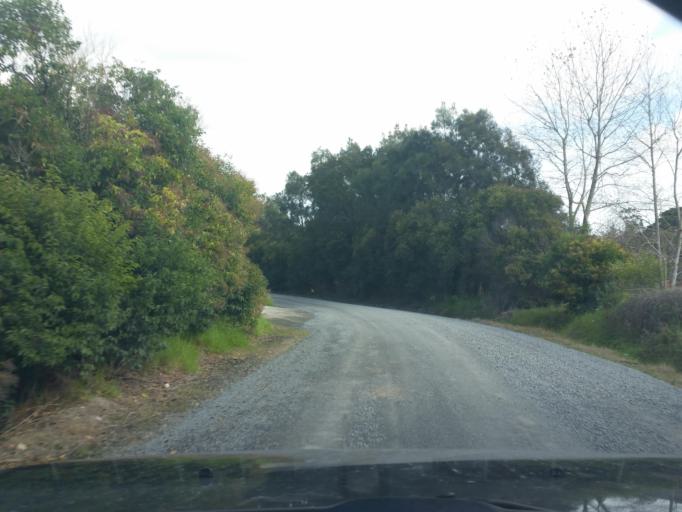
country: NZ
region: Northland
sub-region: Kaipara District
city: Dargaville
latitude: -35.9955
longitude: 173.9521
